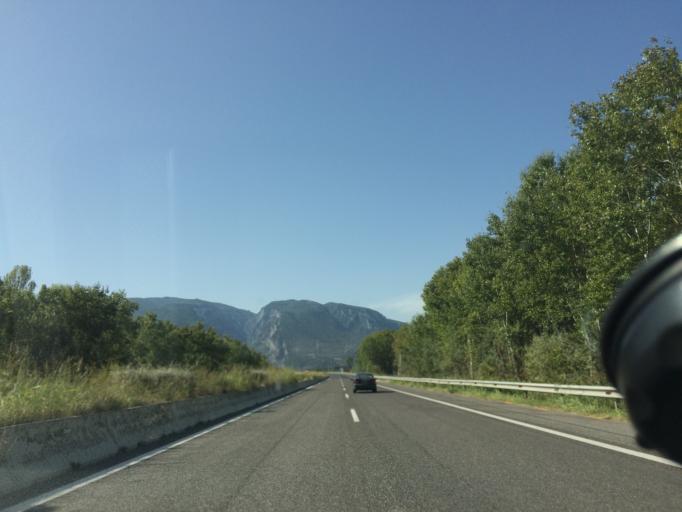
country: GR
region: Thessaly
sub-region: Nomos Larisis
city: Pyrgetos
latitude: 39.9152
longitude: 22.6294
